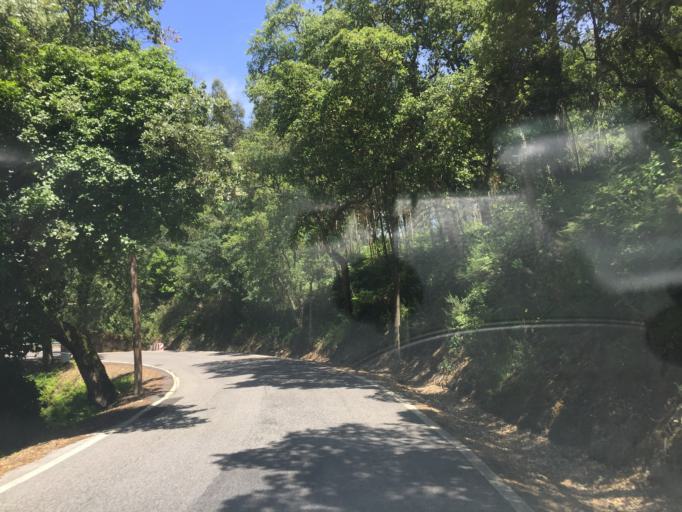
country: PT
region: Lisbon
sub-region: Mafra
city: Venda do Pinheiro
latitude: 38.8920
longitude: -9.2199
